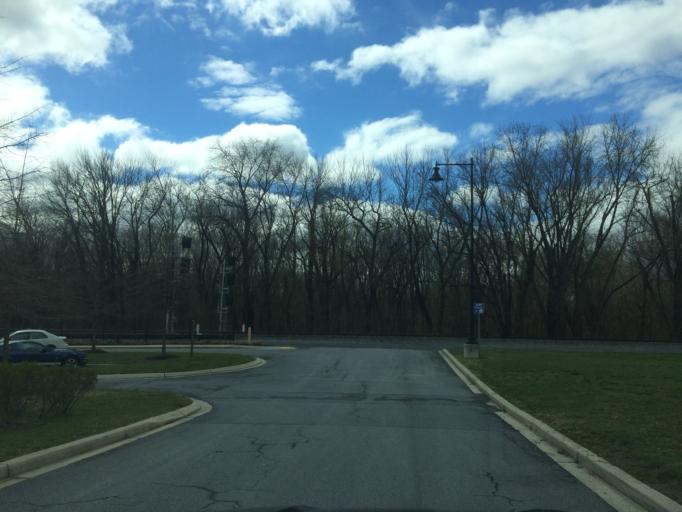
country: US
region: Maryland
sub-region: Frederick County
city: Point of Rocks
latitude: 39.2744
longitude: -77.5384
